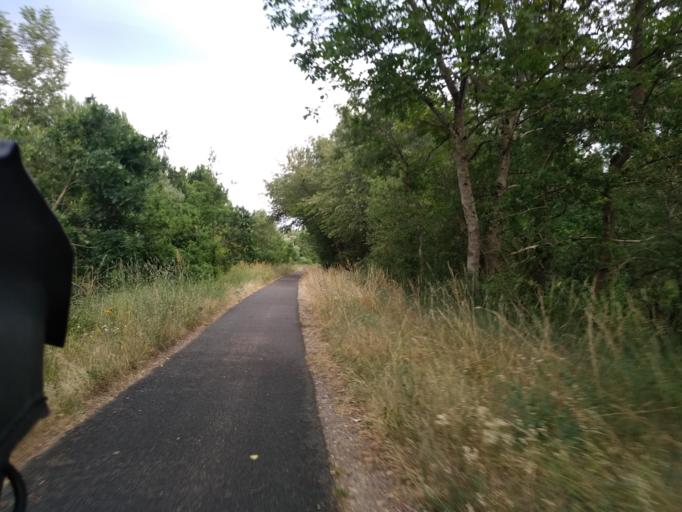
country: FR
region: Auvergne
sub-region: Departement de l'Allier
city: Varennes-sur-Allier
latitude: 46.3468
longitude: 3.3491
